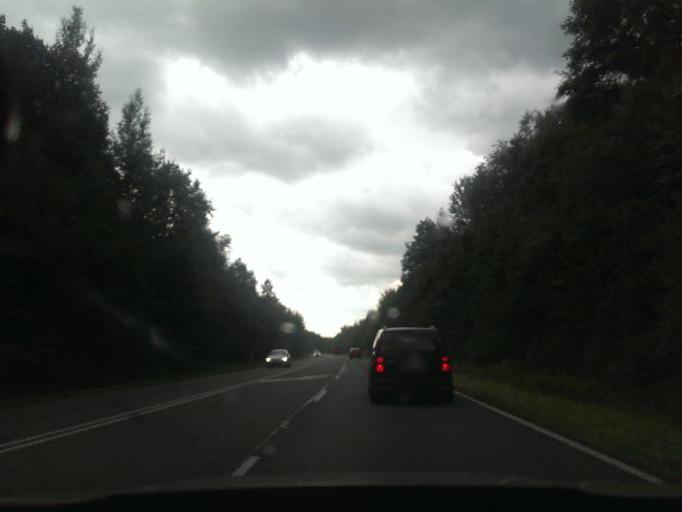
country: DE
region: North Rhine-Westphalia
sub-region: Regierungsbezirk Detmold
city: Schlangen
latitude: 51.8160
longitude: 8.8287
